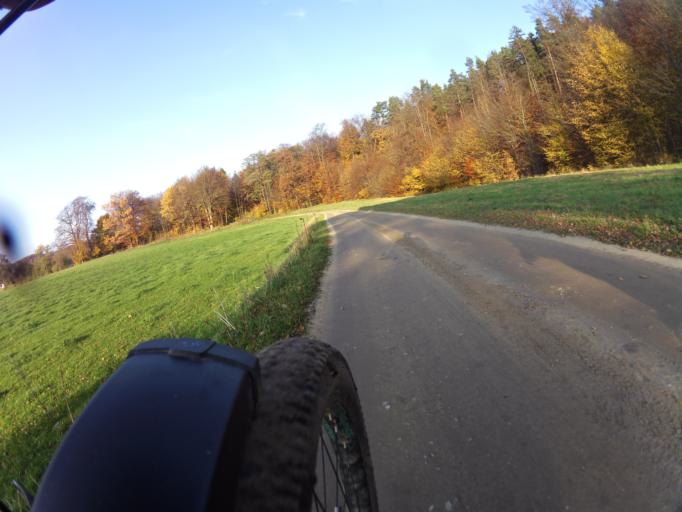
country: PL
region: Pomeranian Voivodeship
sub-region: Powiat pucki
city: Krokowa
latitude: 54.7487
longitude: 18.1959
